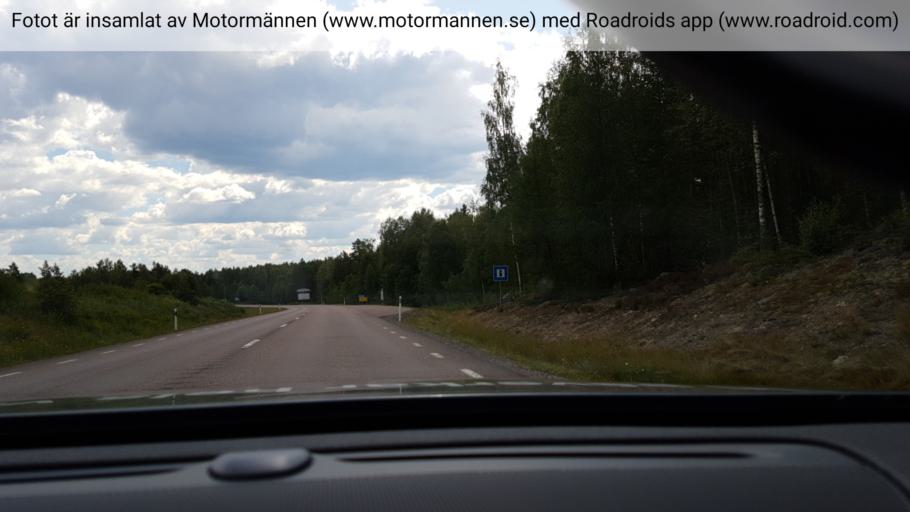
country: SE
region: Dalarna
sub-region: Faluns Kommun
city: Falun
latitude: 60.6324
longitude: 15.5930
